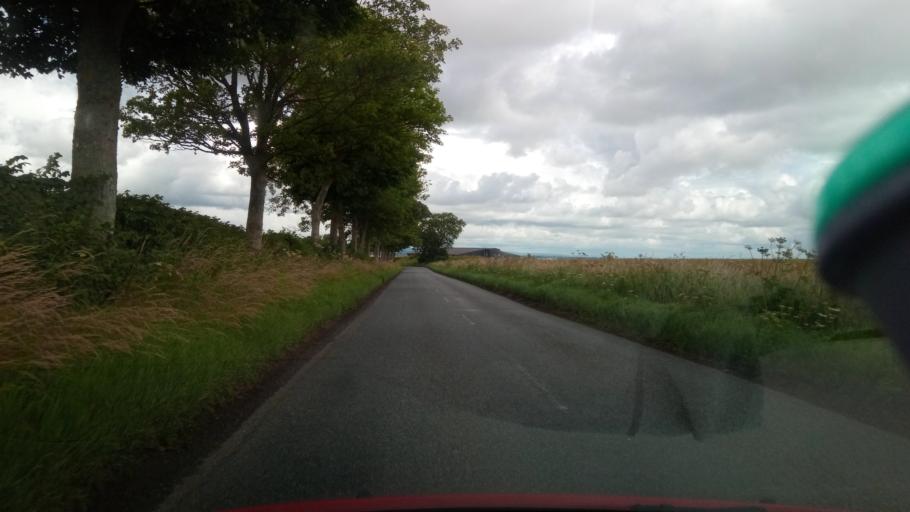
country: GB
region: Scotland
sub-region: The Scottish Borders
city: Kelso
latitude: 55.5759
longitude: -2.4195
